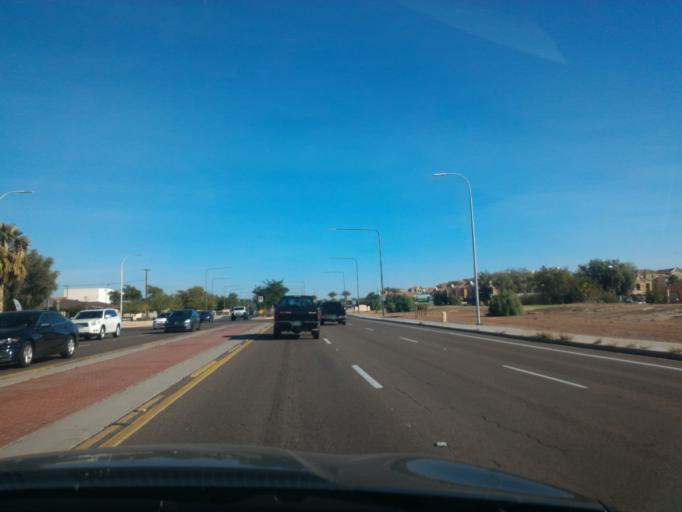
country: US
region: Arizona
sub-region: Maricopa County
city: Chandler
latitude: 33.3060
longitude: -111.8473
